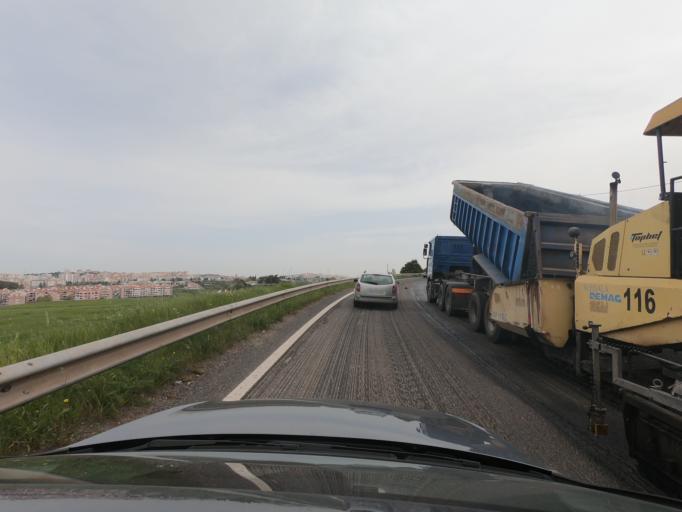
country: PT
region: Lisbon
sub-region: Oeiras
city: Barcarena
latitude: 38.7394
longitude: -9.2782
